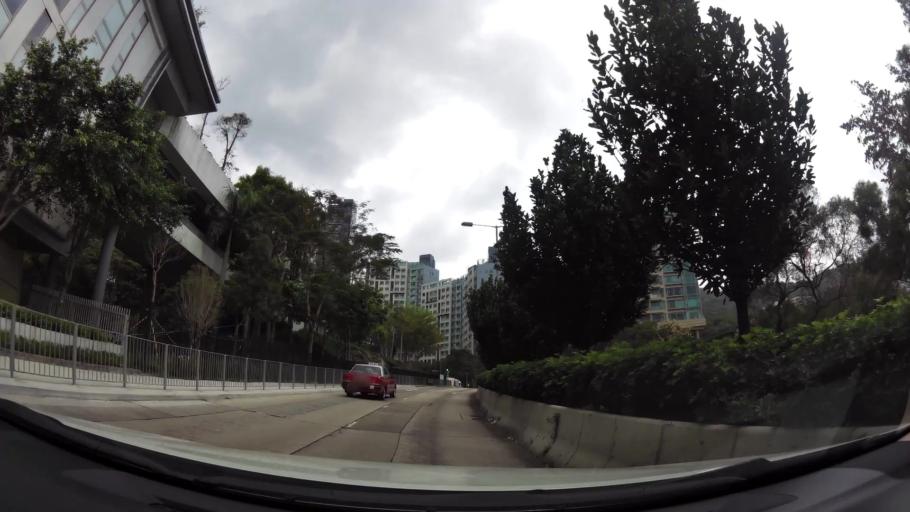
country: HK
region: Sham Shui Po
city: Sham Shui Po
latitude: 22.3388
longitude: 114.1721
